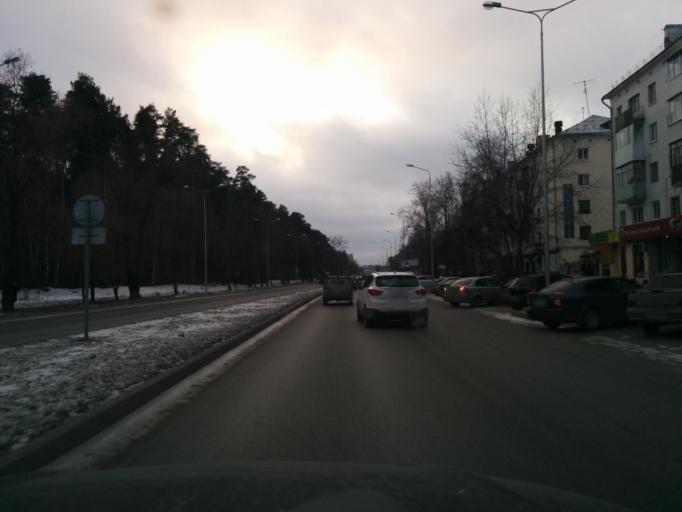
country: RU
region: Perm
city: Kultayevo
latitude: 58.0143
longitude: 55.9761
